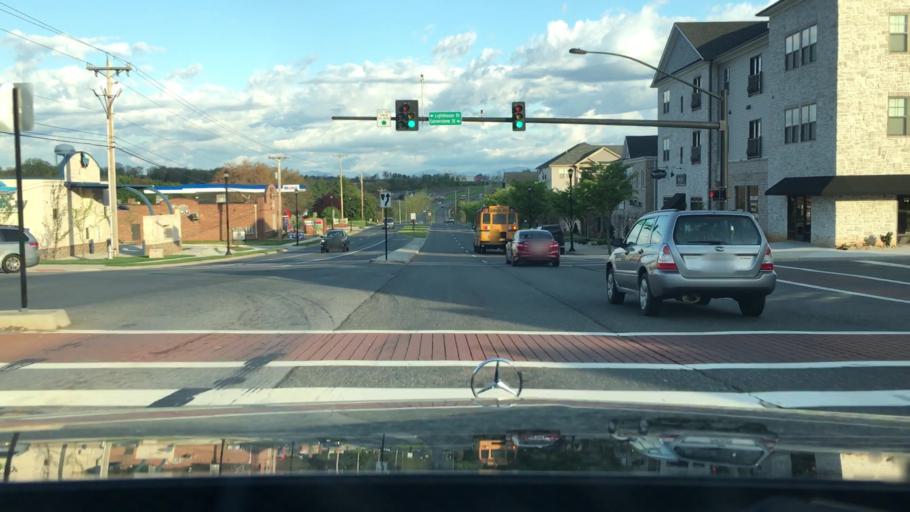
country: US
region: Virginia
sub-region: Campbell County
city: Timberlake
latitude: 37.3393
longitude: -79.2252
